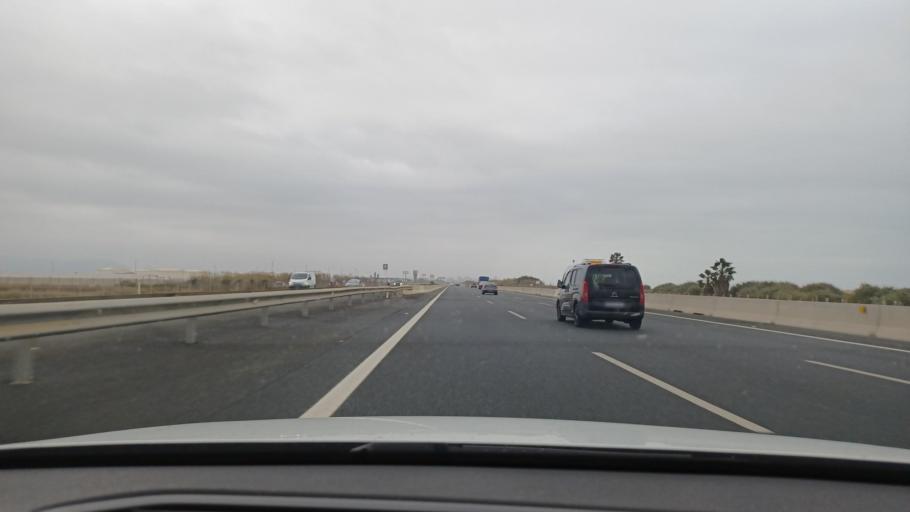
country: ES
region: Valencia
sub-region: Provincia de Valencia
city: Meliana
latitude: 39.5237
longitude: -0.3163
